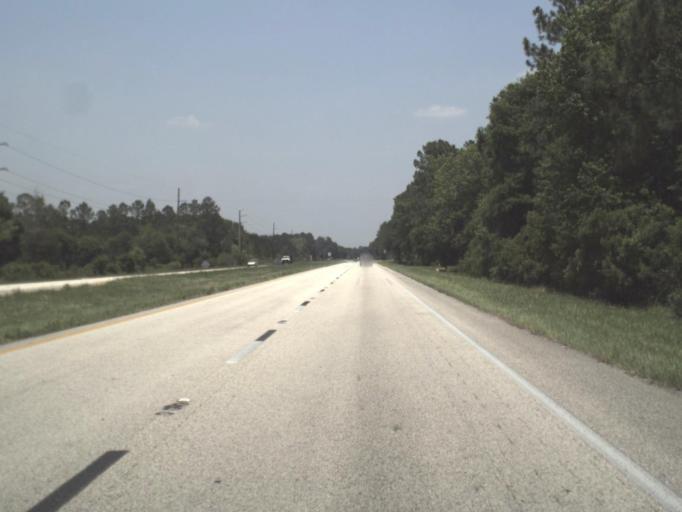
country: US
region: Florida
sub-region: Bradford County
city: Starke
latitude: 30.0091
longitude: -82.0892
